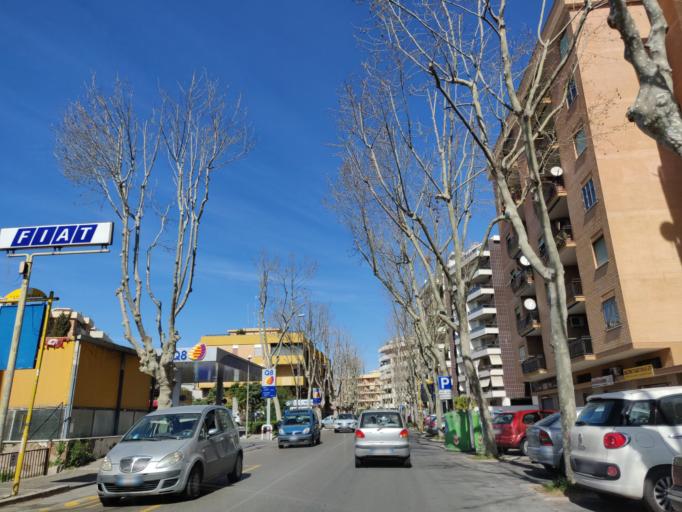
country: IT
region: Latium
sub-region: Citta metropolitana di Roma Capitale
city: Civitavecchia
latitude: 42.0871
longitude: 11.8048
